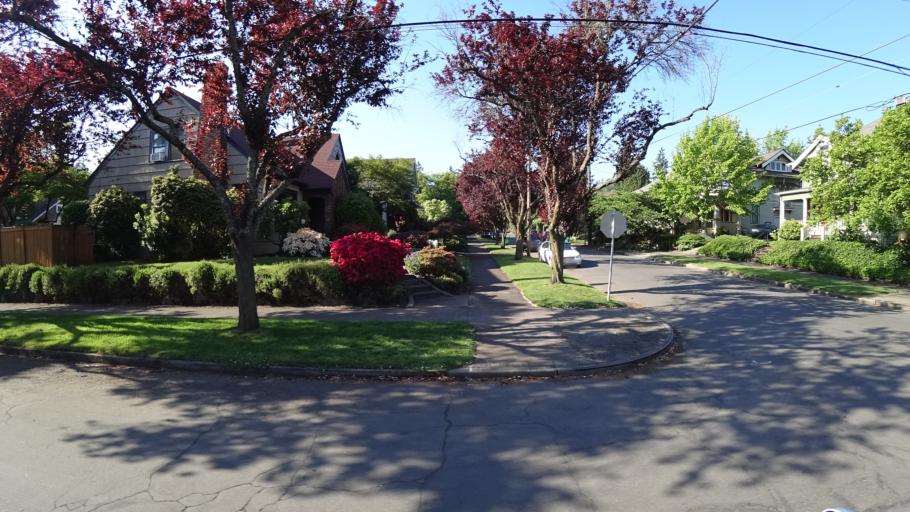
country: US
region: Oregon
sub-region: Multnomah County
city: Portland
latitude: 45.5467
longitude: -122.6350
